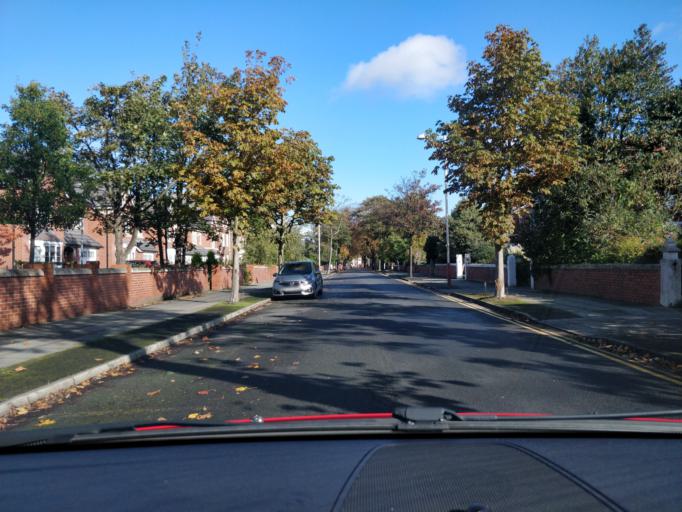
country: GB
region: England
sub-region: Sefton
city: Southport
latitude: 53.6386
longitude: -2.9853
